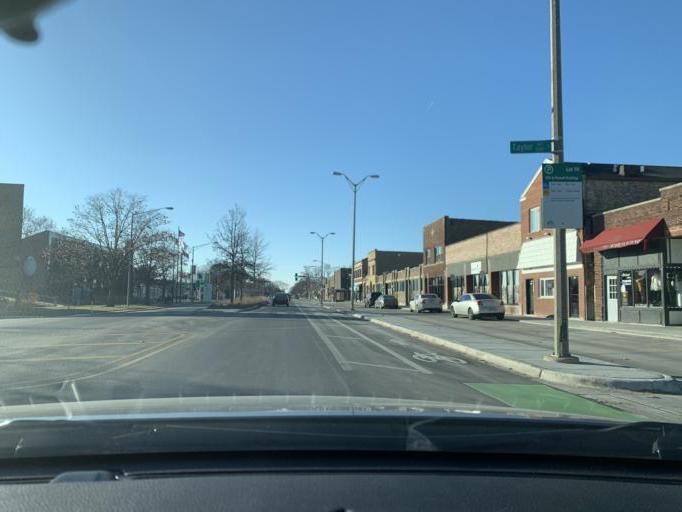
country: US
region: Illinois
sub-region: Cook County
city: Oak Park
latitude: 41.8801
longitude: -87.7780
